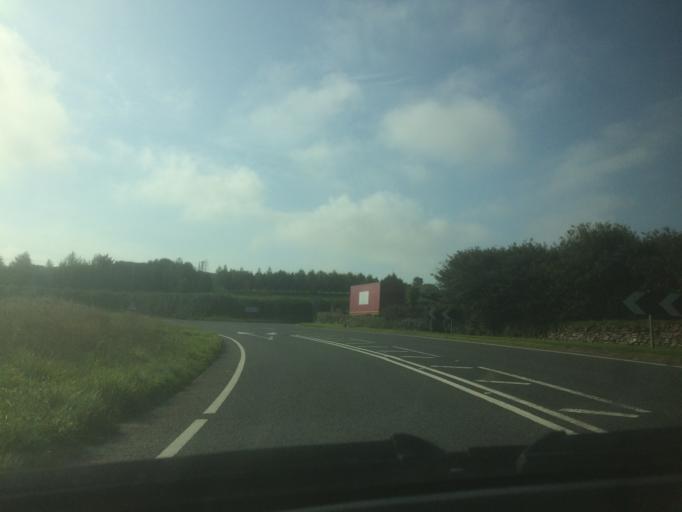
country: GB
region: England
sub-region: Cornwall
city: Saltash
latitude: 50.4298
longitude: -4.2586
